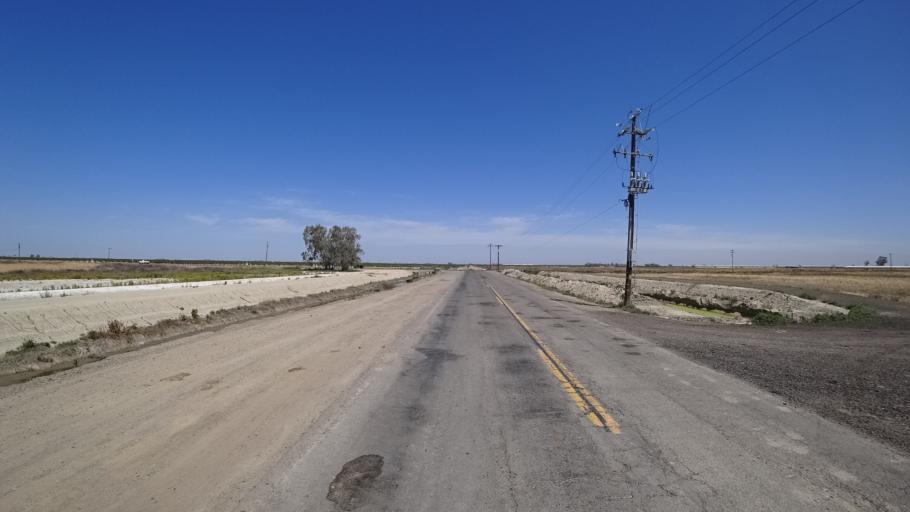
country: US
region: California
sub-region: Kings County
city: Stratford
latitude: 36.1881
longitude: -119.7176
